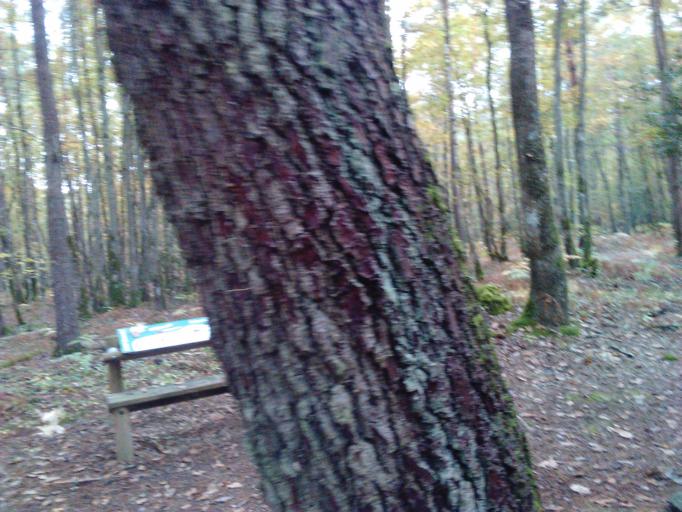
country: FR
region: Centre
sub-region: Departement du Loir-et-Cher
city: Naveil
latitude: 47.8200
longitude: 1.0320
